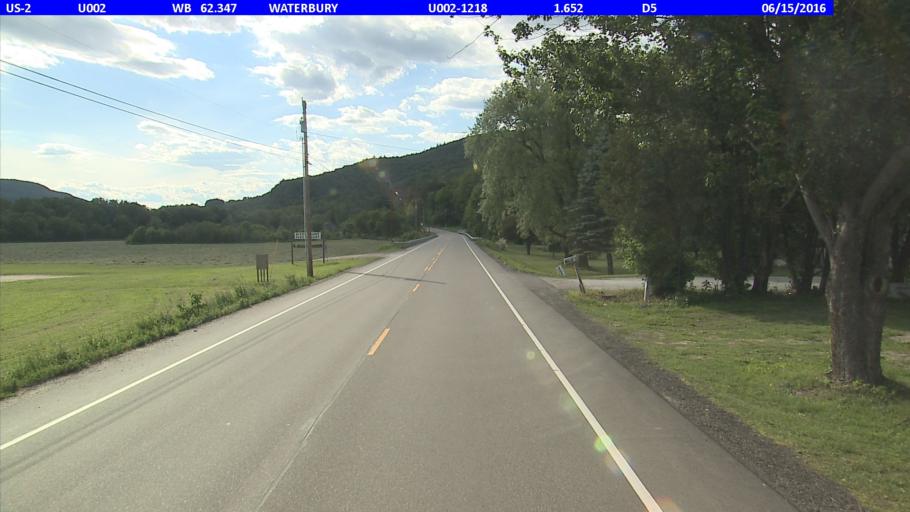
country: US
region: Vermont
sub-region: Washington County
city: Waterbury
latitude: 44.3574
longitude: -72.7945
